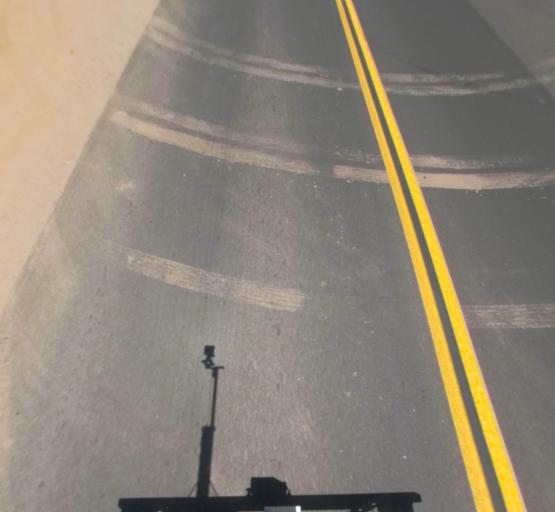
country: US
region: California
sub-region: Madera County
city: Madera
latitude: 36.9868
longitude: -120.0429
